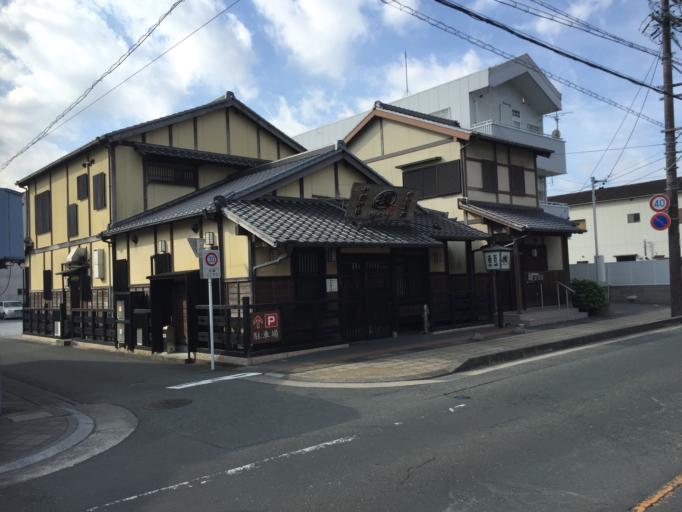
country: JP
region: Shizuoka
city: Kosai-shi
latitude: 34.6942
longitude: 137.5629
